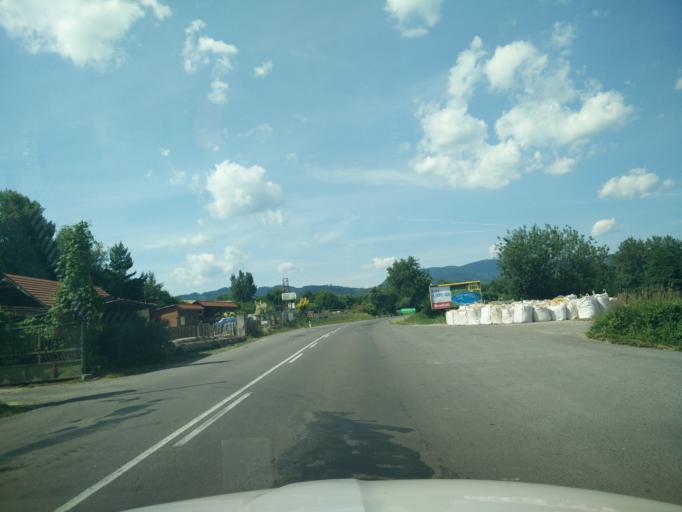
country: SK
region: Nitriansky
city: Prievidza
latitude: 48.8821
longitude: 18.6382
